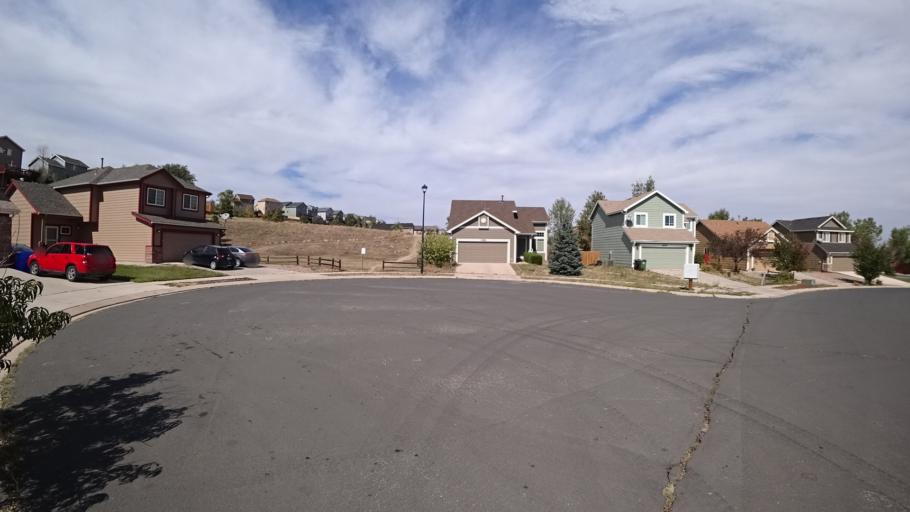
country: US
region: Colorado
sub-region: El Paso County
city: Cimarron Hills
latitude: 38.9005
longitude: -104.7162
